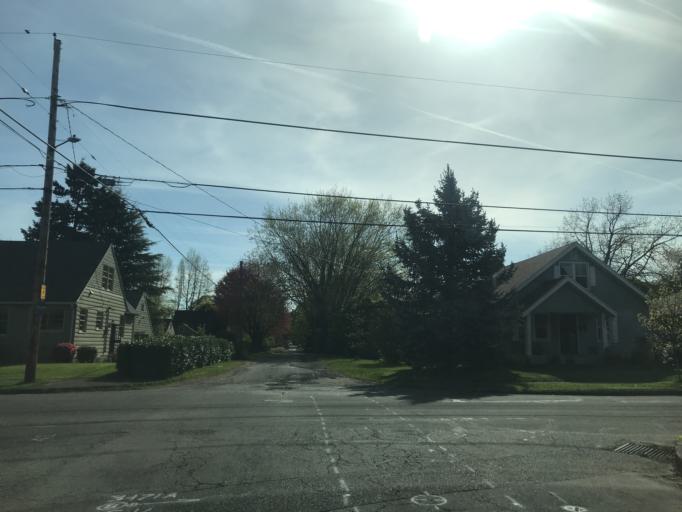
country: US
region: Oregon
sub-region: Multnomah County
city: Lents
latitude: 45.4987
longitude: -122.5875
